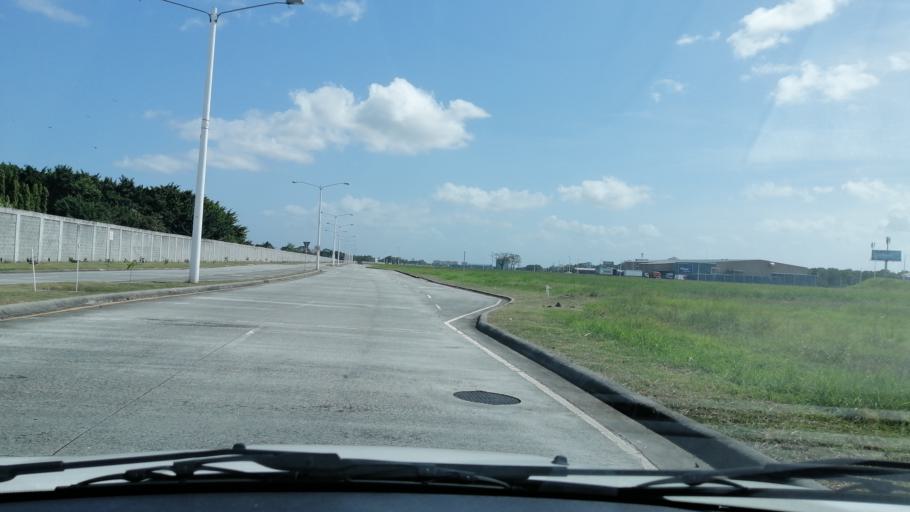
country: PA
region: Panama
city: San Miguelito
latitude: 9.0348
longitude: -79.4453
